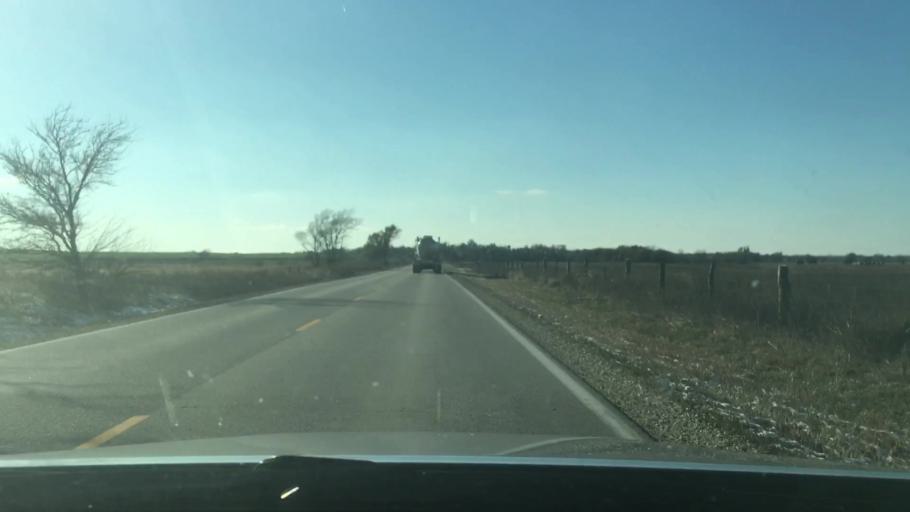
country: US
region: Kansas
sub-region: Reno County
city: Nickerson
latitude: 38.1449
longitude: -98.1278
